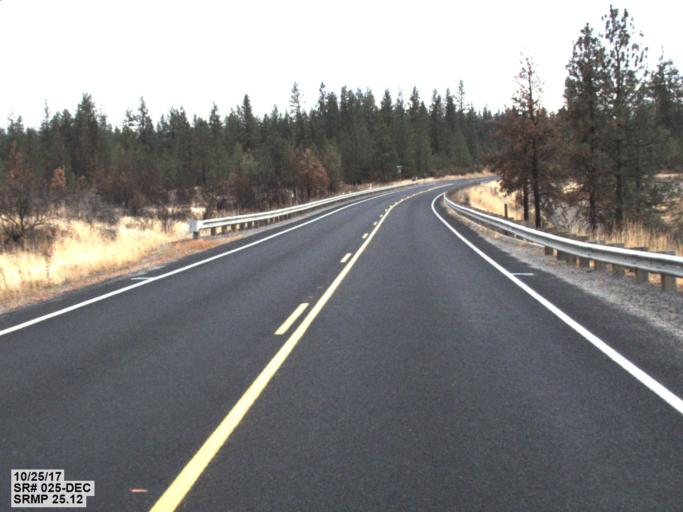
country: US
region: Washington
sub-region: Lincoln County
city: Davenport
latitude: 47.9180
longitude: -118.3308
